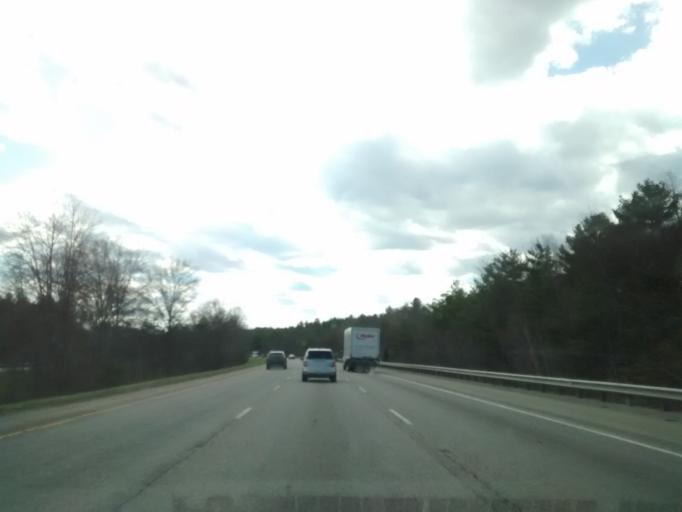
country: US
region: Massachusetts
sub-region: Worcester County
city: Northborough
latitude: 42.3418
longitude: -71.6463
